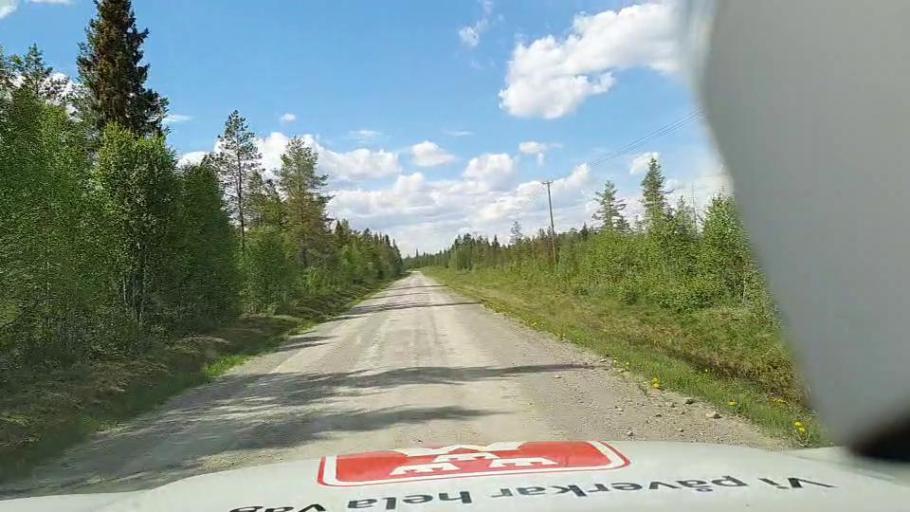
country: SE
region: Vaesterbotten
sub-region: Vilhelmina Kommun
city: Sjoberg
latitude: 64.5428
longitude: 15.6530
